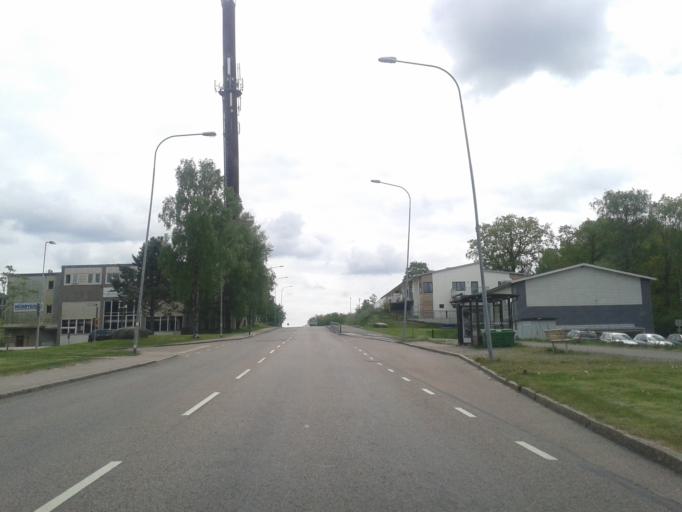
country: SE
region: Vaestra Goetaland
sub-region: Kungalvs Kommun
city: Kungalv
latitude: 57.8703
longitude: 11.9509
